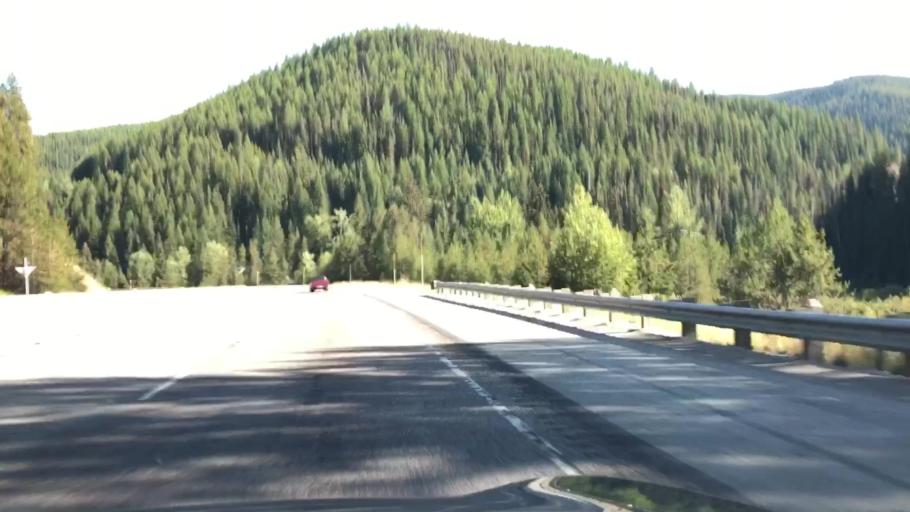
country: US
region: Montana
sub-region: Sanders County
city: Thompson Falls
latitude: 47.4168
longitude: -115.5892
